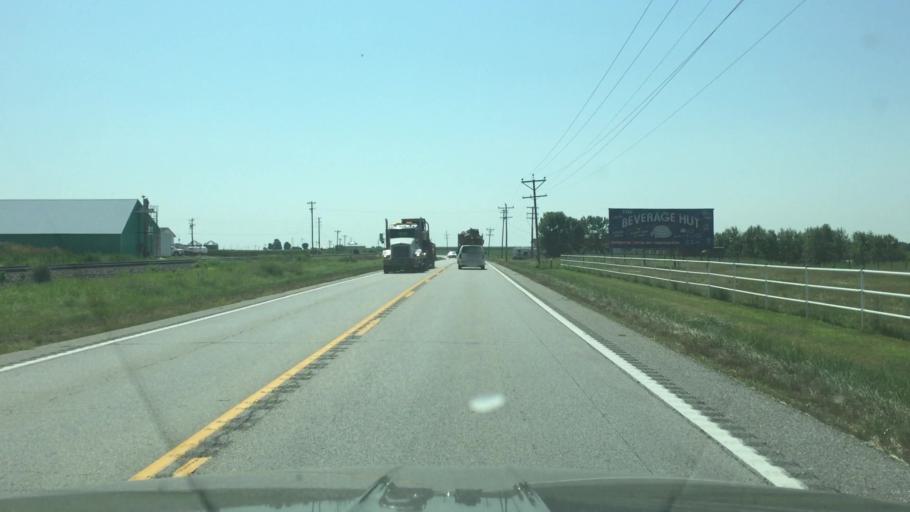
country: US
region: Missouri
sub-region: Moniteau County
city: Tipton
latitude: 38.6686
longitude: -92.8429
